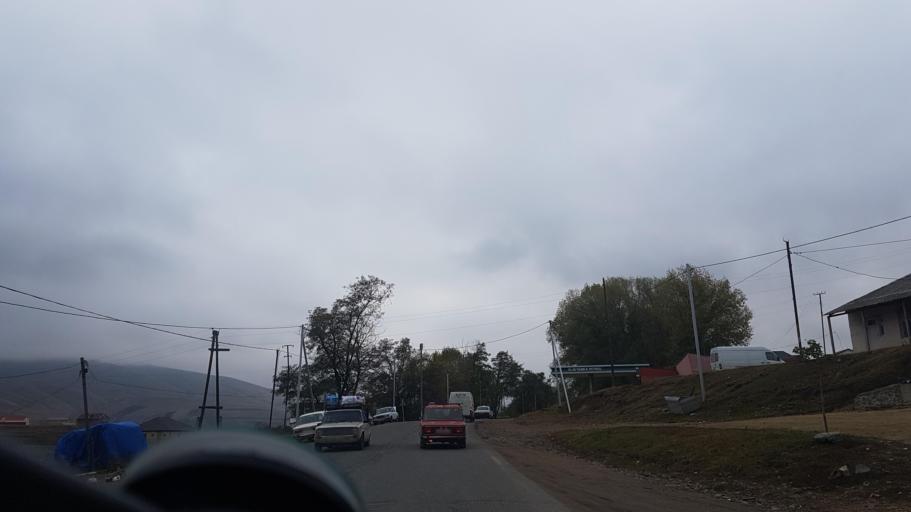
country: AZ
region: Gadabay Rayon
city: Ariqdam
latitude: 40.6521
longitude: 45.8080
